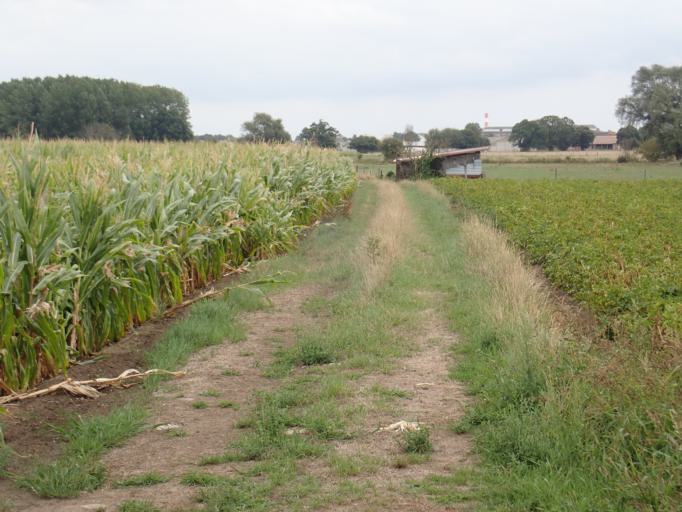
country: BE
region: Flanders
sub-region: Provincie Vlaams-Brabant
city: Kapelle-op-den-Bos
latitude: 51.0053
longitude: 4.3373
